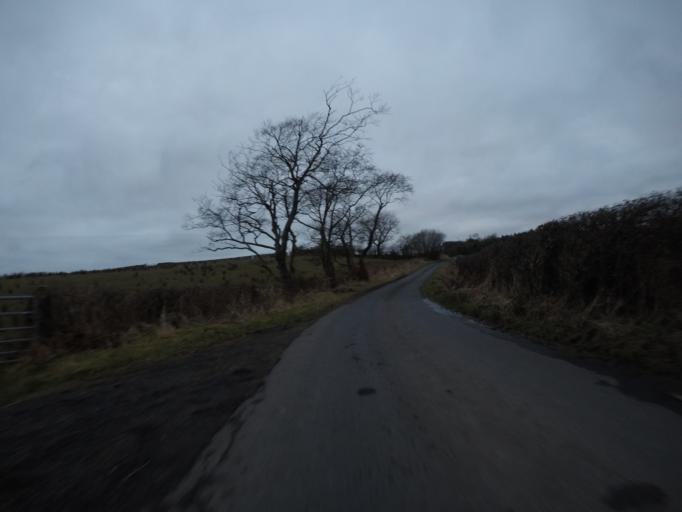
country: GB
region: Scotland
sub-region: North Ayrshire
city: Kilwinning
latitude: 55.6747
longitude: -4.7250
